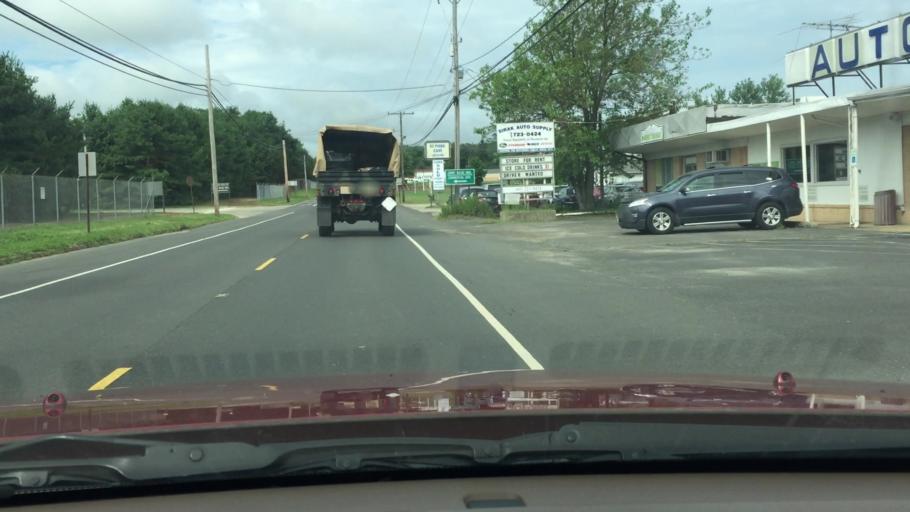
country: US
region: New Jersey
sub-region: Burlington County
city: Fort Dix
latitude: 40.0339
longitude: -74.6316
